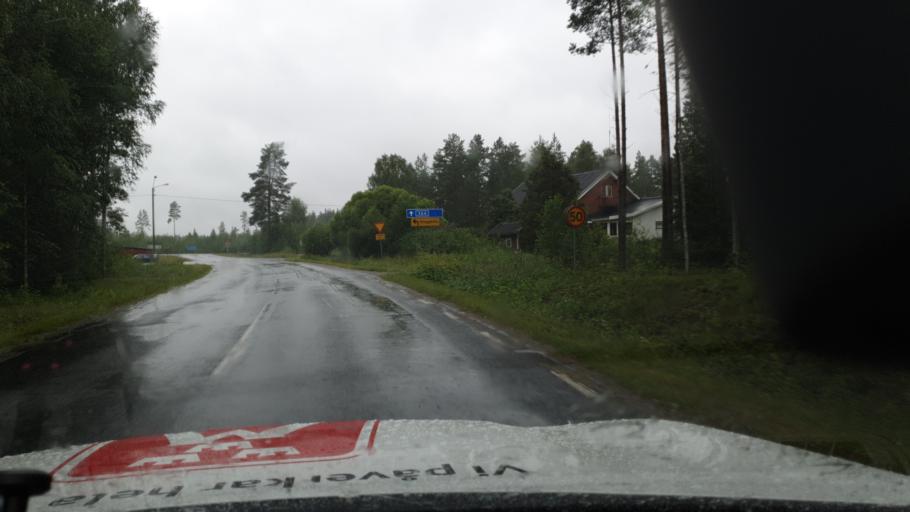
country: SE
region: Vaesterbotten
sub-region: Skelleftea Kommun
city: Viken
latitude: 64.5891
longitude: 20.9420
